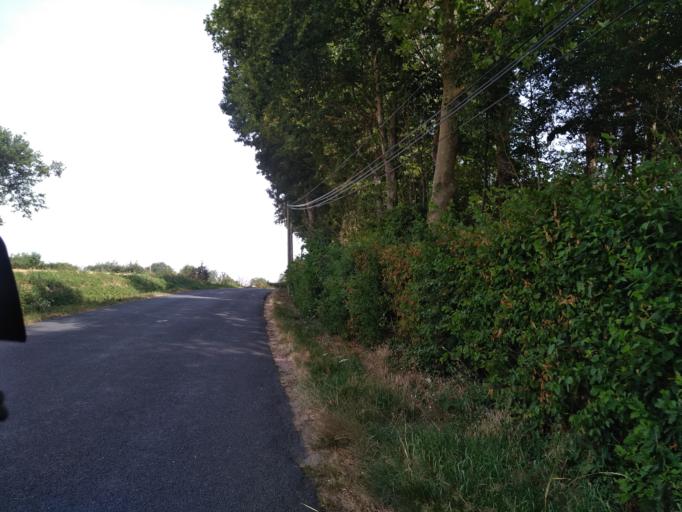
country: FR
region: Auvergne
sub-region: Departement de l'Allier
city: Molinet
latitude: 46.4282
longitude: 3.9746
